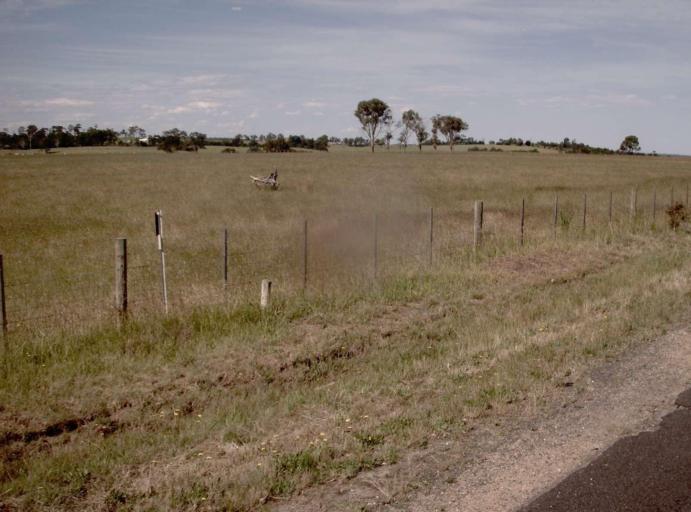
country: AU
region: Victoria
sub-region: East Gippsland
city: Bairnsdale
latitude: -37.8206
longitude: 147.7771
